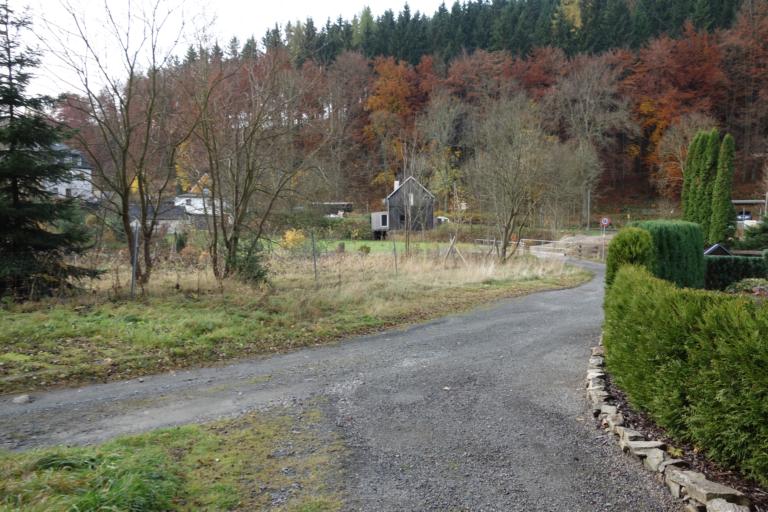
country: DE
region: Saxony
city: Barenstein
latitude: 50.5142
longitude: 13.0415
